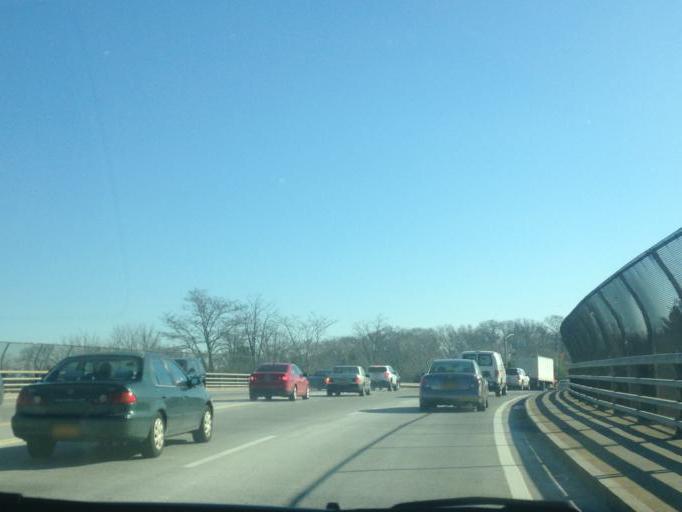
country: US
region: New York
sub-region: Suffolk County
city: Patchogue
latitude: 40.7776
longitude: -73.0304
